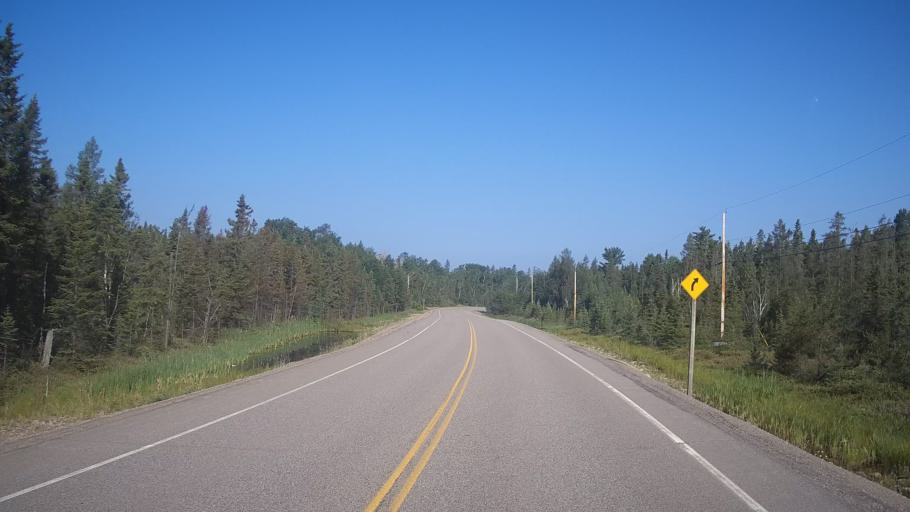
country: CA
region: Ontario
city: Rayside-Balfour
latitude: 46.7308
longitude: -81.5844
